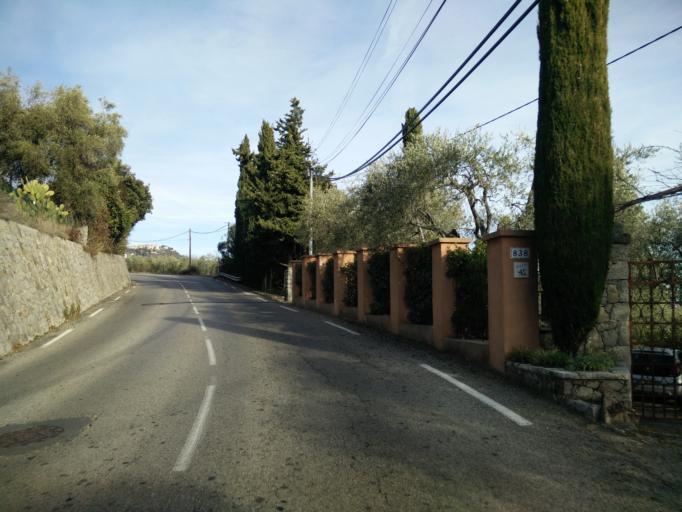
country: FR
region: Provence-Alpes-Cote d'Azur
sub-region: Departement des Alpes-Maritimes
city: Speracedes
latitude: 43.6407
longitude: 6.8536
